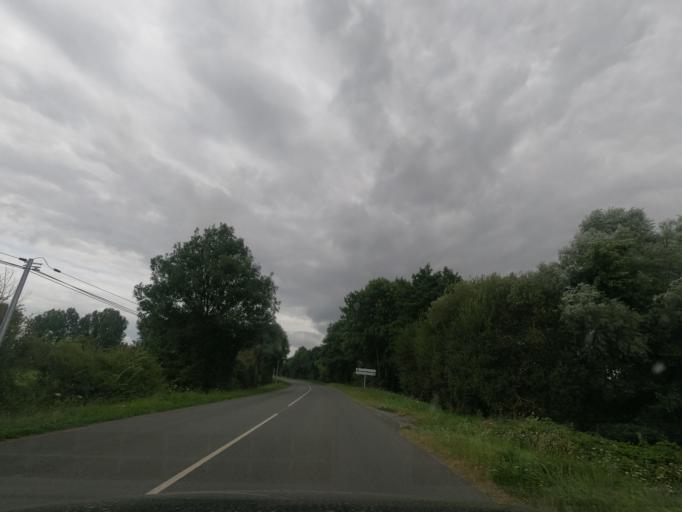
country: FR
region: Lower Normandy
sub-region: Departement de l'Orne
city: Ecouche
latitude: 48.7143
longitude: -0.1060
